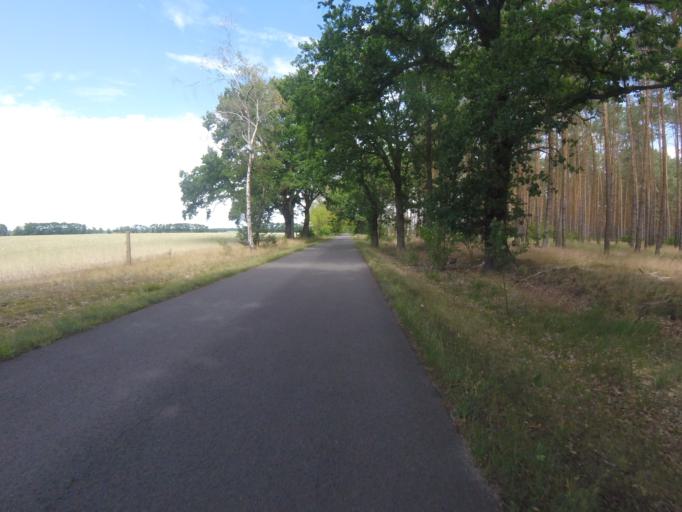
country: DE
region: Brandenburg
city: Bestensee
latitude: 52.2259
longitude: 13.7064
